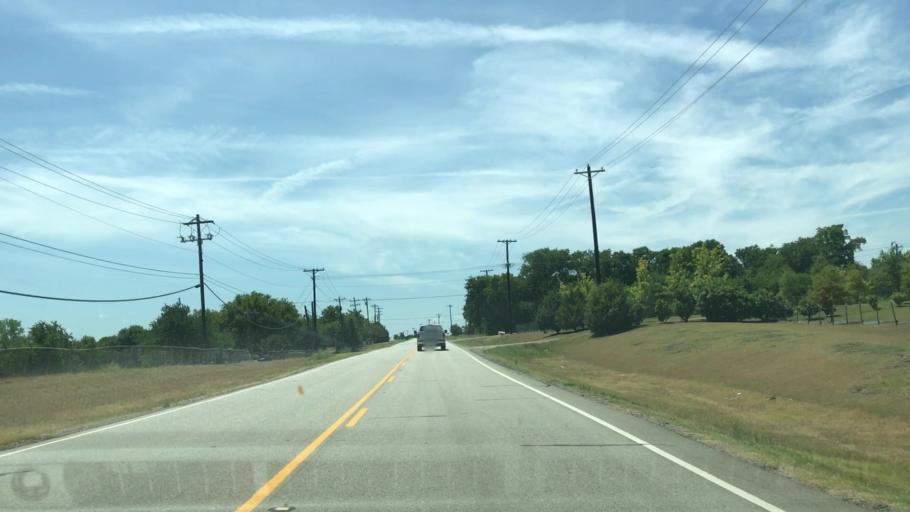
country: US
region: Texas
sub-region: Collin County
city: Saint Paul
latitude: 33.0445
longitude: -96.5498
